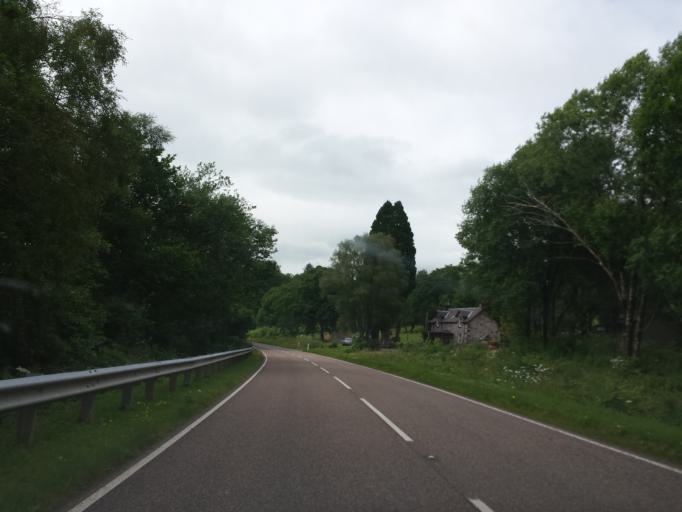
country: GB
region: Scotland
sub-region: Highland
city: Fort William
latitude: 56.8590
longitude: -5.3170
